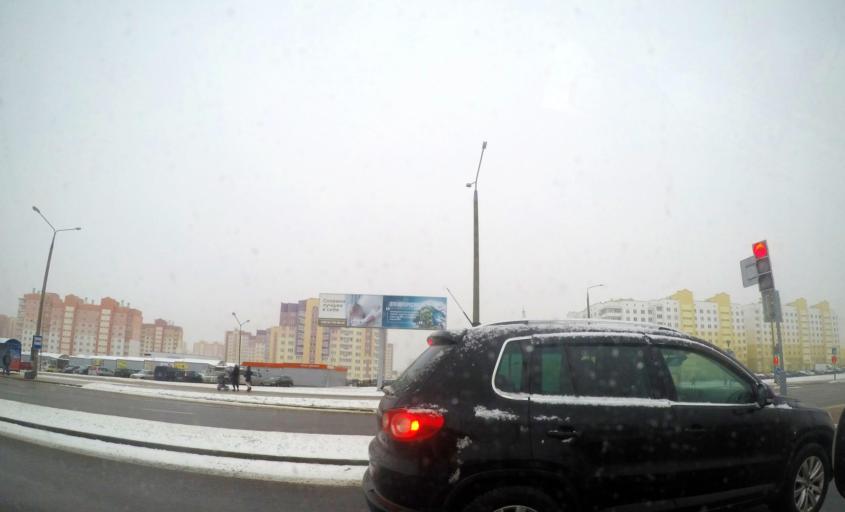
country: BY
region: Grodnenskaya
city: Hrodna
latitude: 53.6245
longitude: 23.8132
